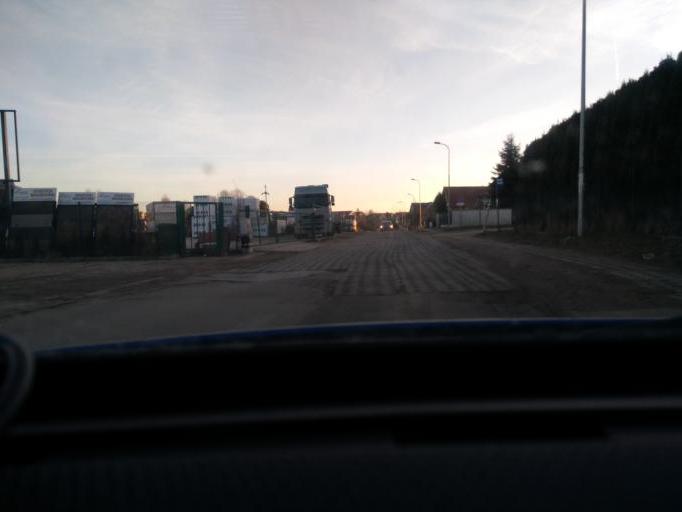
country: PL
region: Pomeranian Voivodeship
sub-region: Powiat kartuski
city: Banino
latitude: 54.3931
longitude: 18.3836
